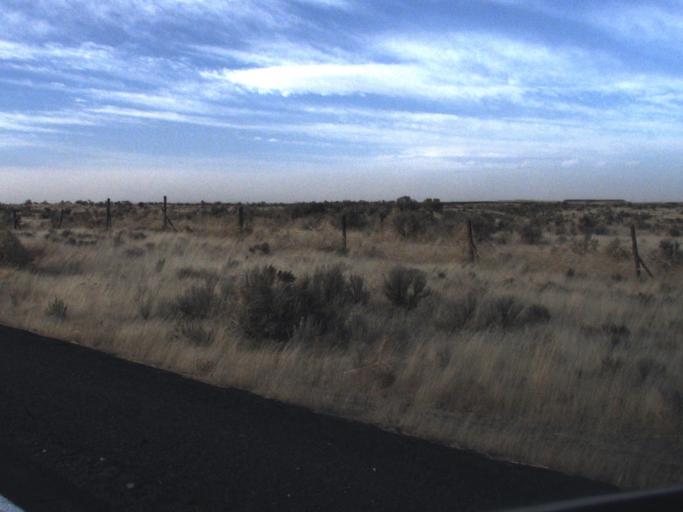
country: US
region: Washington
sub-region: Grant County
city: Warden
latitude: 47.3204
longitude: -118.8601
